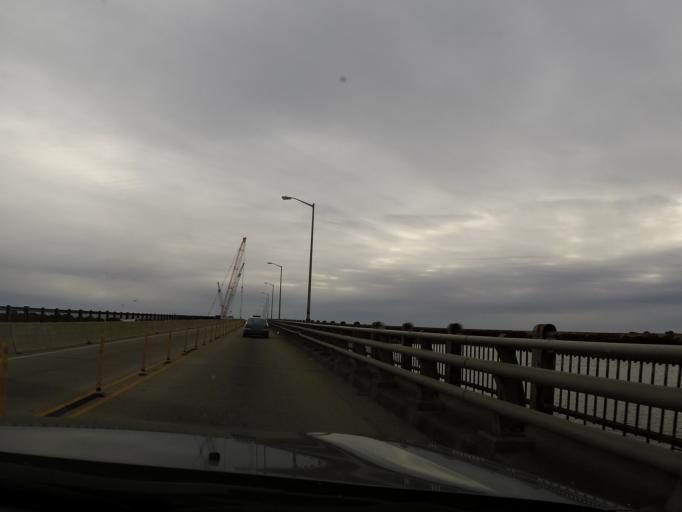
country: US
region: Virginia
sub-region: City of Portsmouth
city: Portsmouth Heights
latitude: 36.8439
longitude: -76.3653
